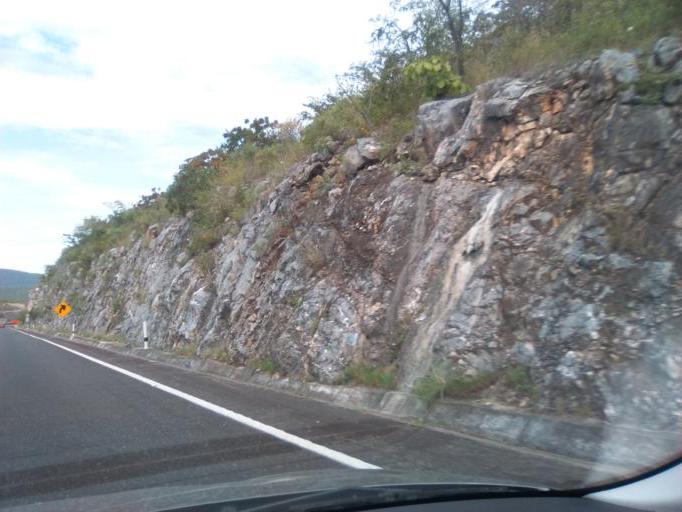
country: MX
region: Guerrero
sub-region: Eduardo Neri
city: Axaxacualco
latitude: 17.7929
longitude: -99.4849
